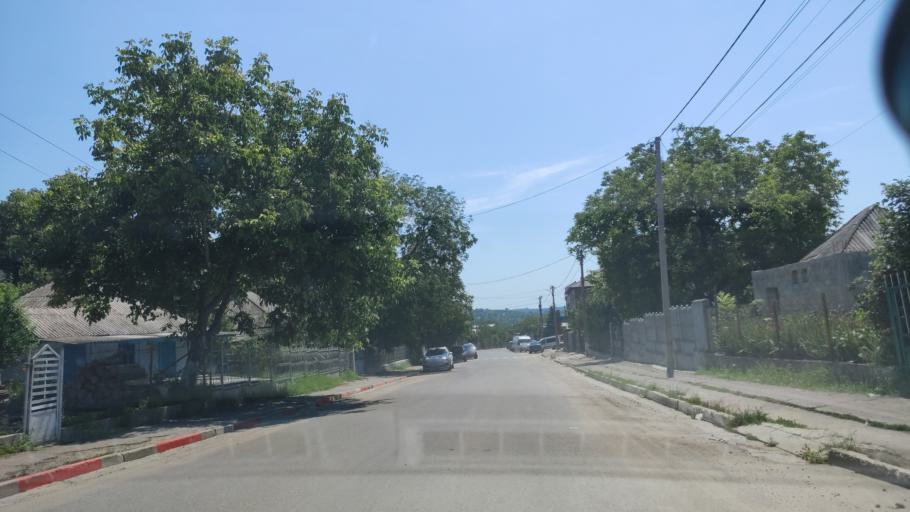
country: MD
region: Raionul Soroca
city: Soroca
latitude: 48.1677
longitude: 28.3020
